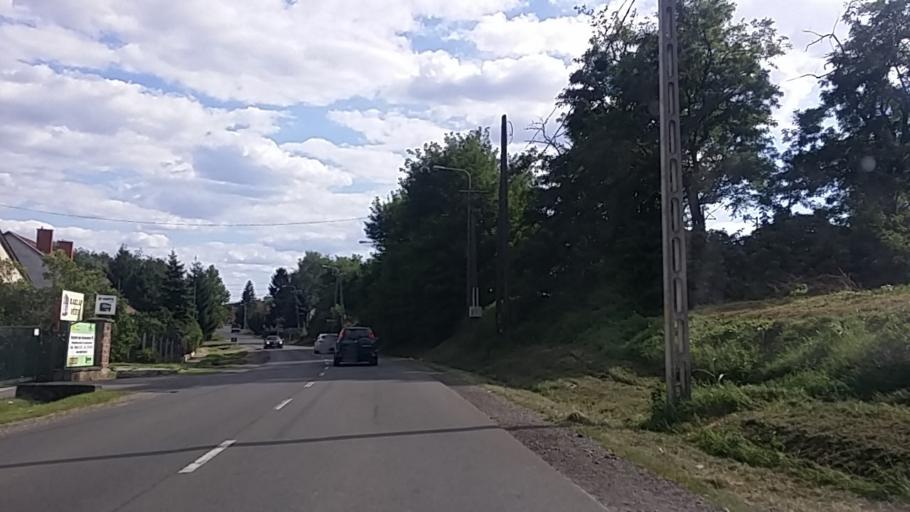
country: HU
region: Baranya
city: Sasd
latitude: 46.2595
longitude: 18.1055
